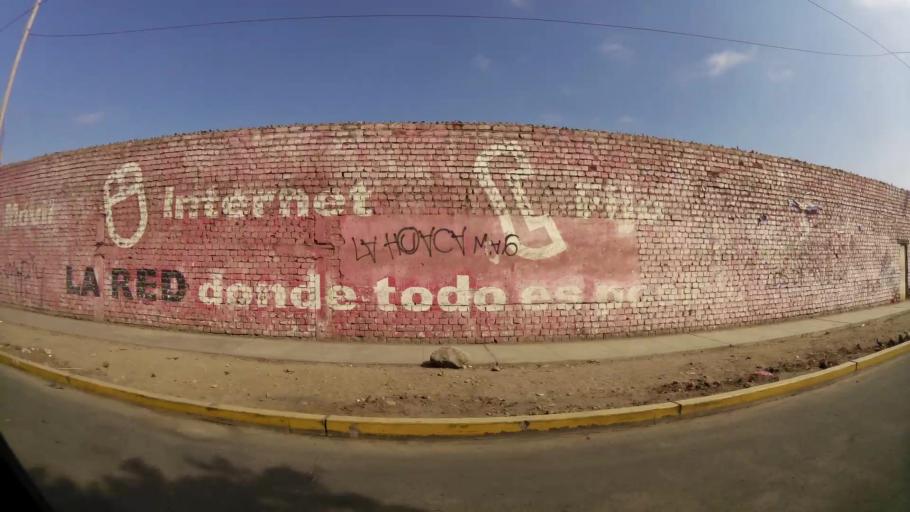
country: PE
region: La Libertad
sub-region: Provincia de Trujillo
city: Trujillo
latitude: -8.1124
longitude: -79.0061
